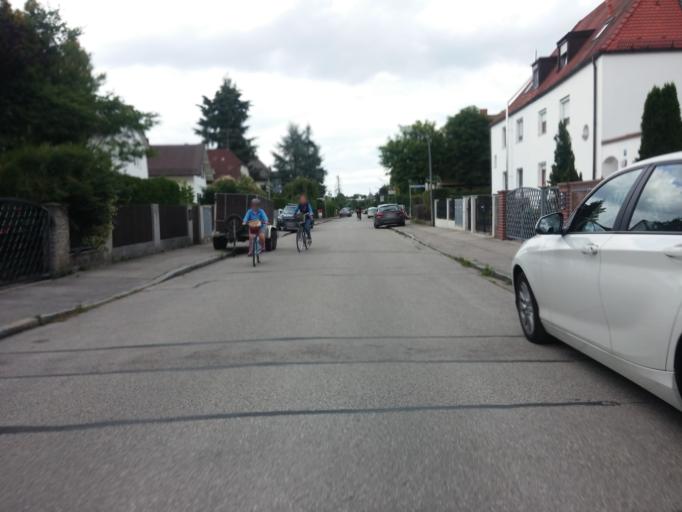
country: DE
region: Bavaria
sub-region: Upper Bavaria
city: Bogenhausen
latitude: 48.1500
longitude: 11.6452
